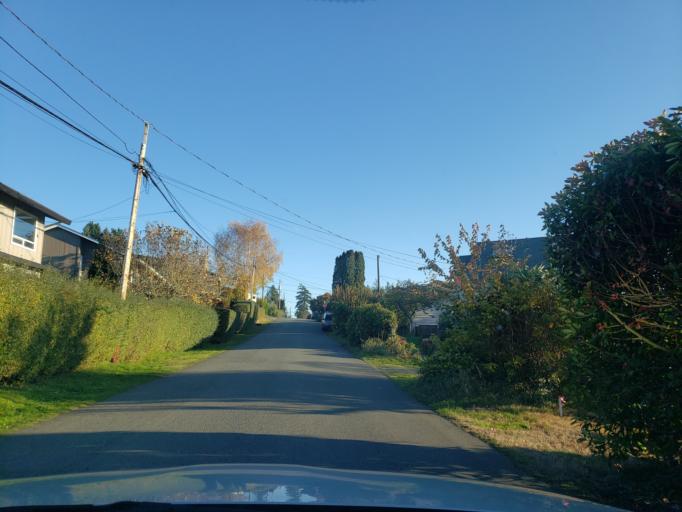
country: US
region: Washington
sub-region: Snohomish County
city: Woodway
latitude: 47.7767
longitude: -122.3865
